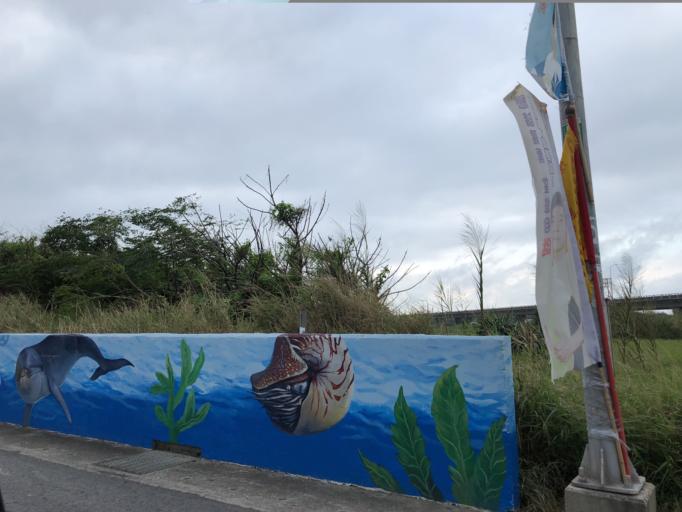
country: TW
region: Taiwan
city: Taoyuan City
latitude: 25.1110
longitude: 121.2425
